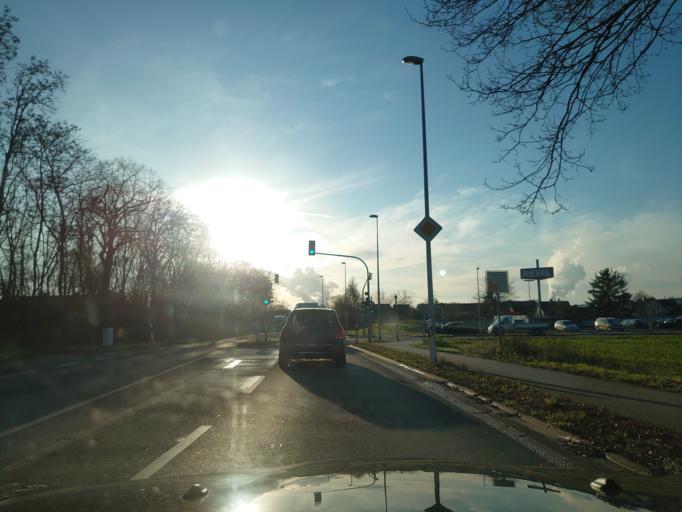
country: DE
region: North Rhine-Westphalia
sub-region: Regierungsbezirk Dusseldorf
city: Dormagen
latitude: 51.0831
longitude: 6.7811
